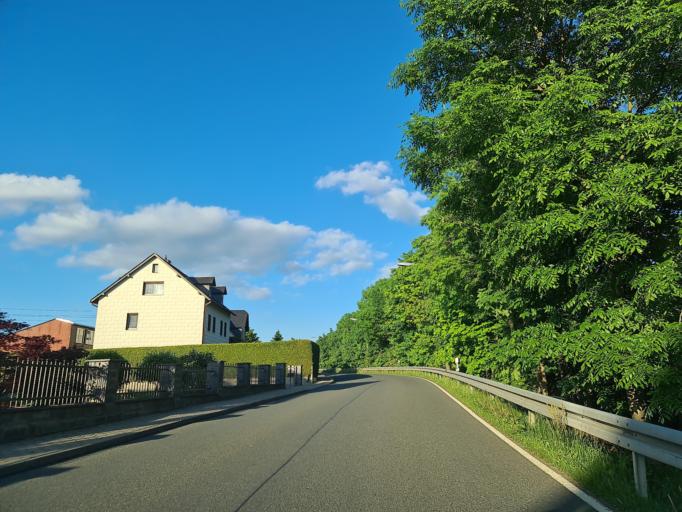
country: DE
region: Saxony
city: Reuth
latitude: 50.4765
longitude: 11.9558
